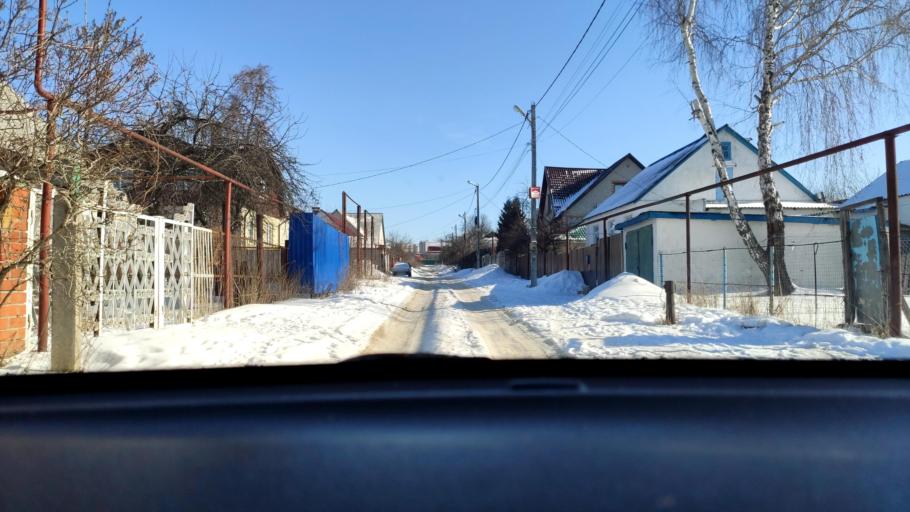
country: RU
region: Voronezj
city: Podgornoye
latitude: 51.7293
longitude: 39.1480
